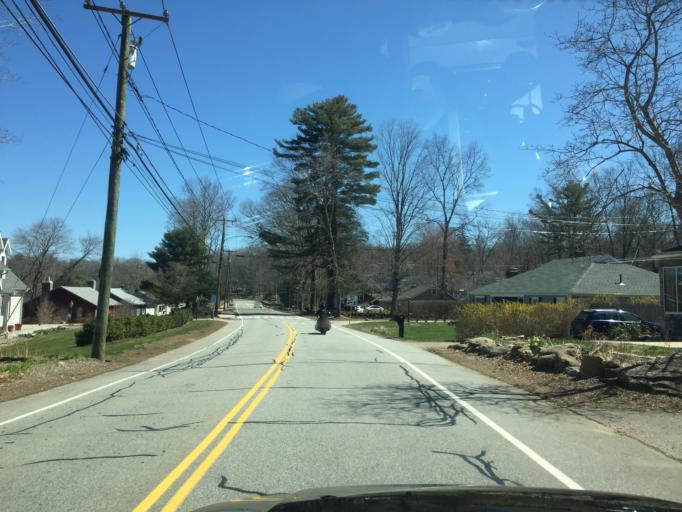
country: US
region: Connecticut
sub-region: Hartford County
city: Terramuggus
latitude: 41.6360
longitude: -72.4708
